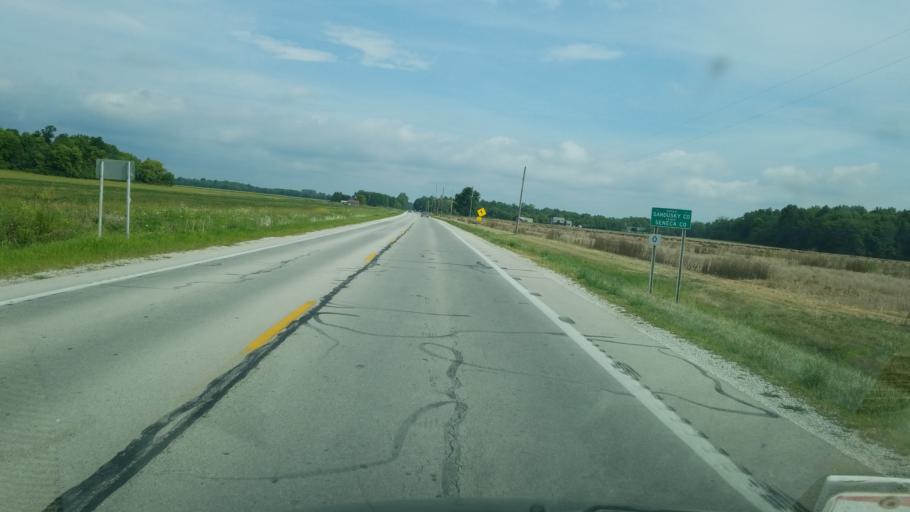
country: US
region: Ohio
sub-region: Sandusky County
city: Ballville
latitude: 41.2553
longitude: -83.1676
